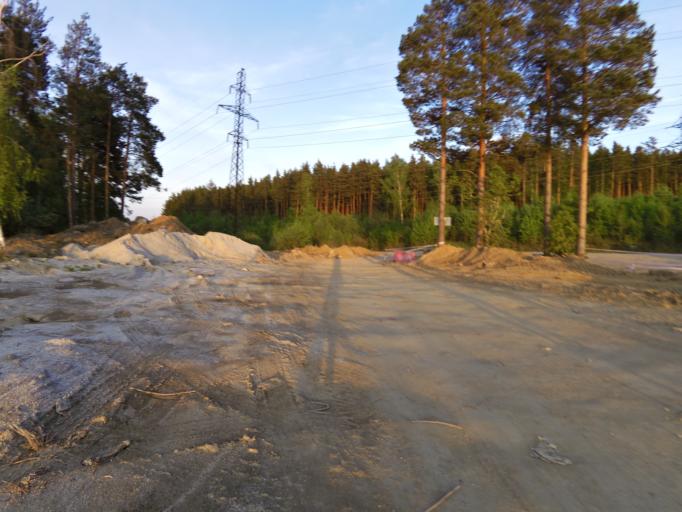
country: RU
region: Sverdlovsk
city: Shirokaya Rechka
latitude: 56.8349
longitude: 60.4686
